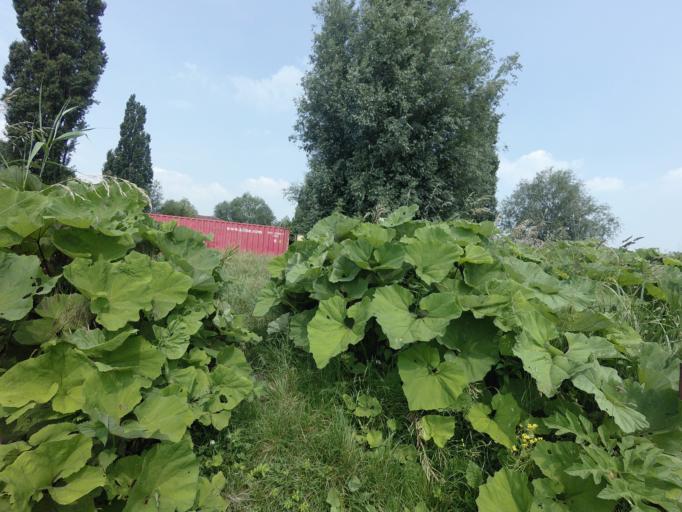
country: NL
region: South Holland
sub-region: Gemeente Krimpen aan den IJssel
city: Krimpen aan den IJssel
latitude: 51.9745
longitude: 4.6294
